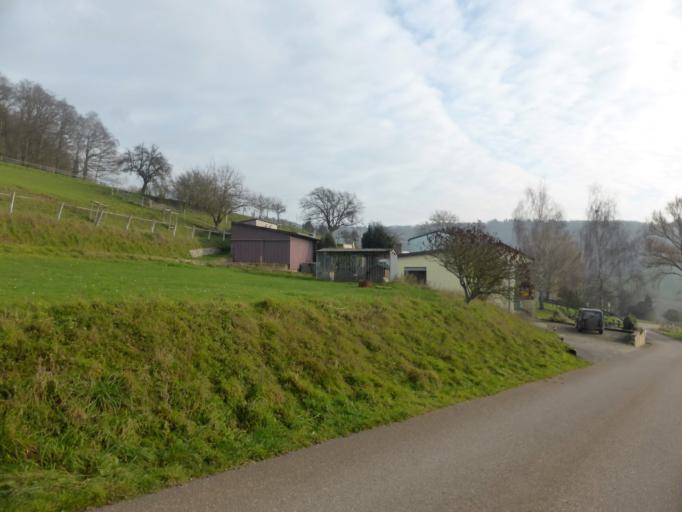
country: LU
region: Luxembourg
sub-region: Canton de Mersch
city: Mersch
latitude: 49.7619
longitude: 6.1237
